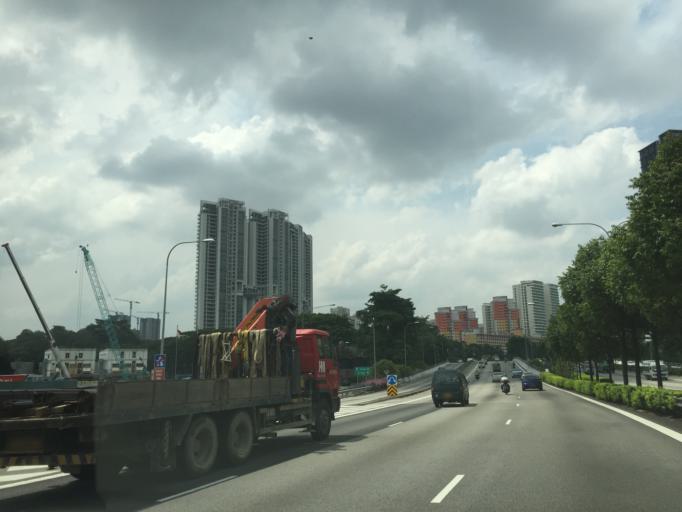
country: SG
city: Singapore
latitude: 1.3277
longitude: 103.8381
